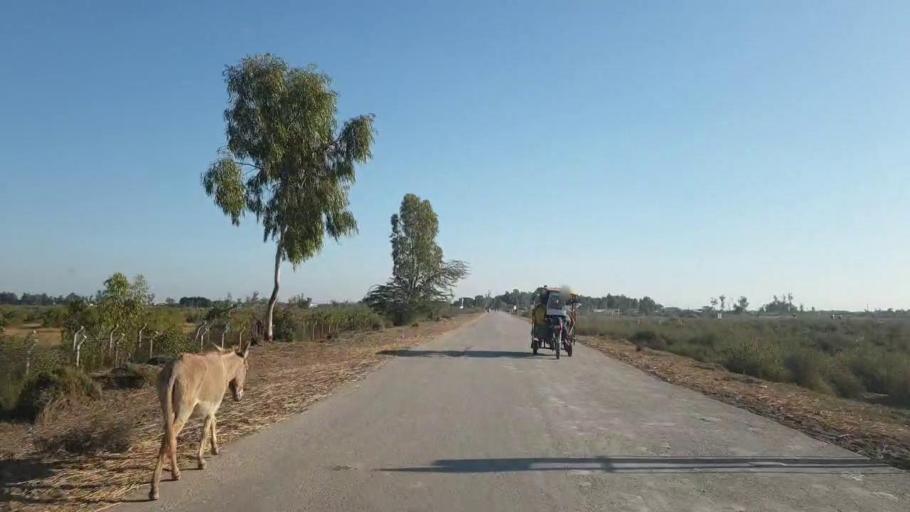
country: PK
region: Sindh
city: Dokri
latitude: 27.3347
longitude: 68.1289
